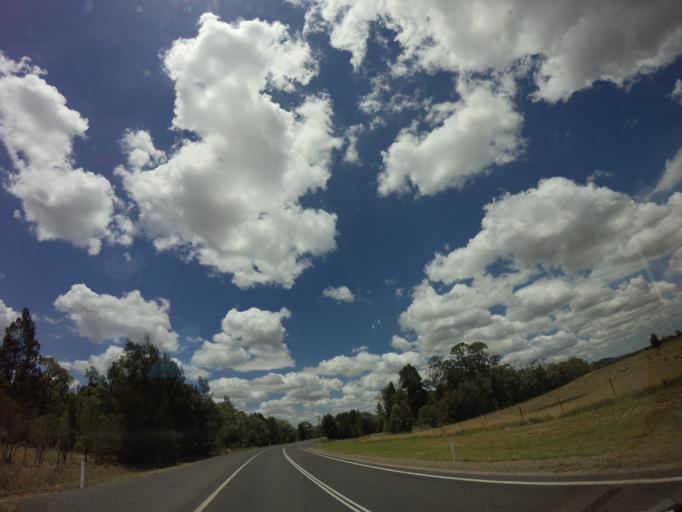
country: AU
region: Queensland
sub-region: Western Downs
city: Dalby
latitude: -27.9667
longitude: 151.1139
